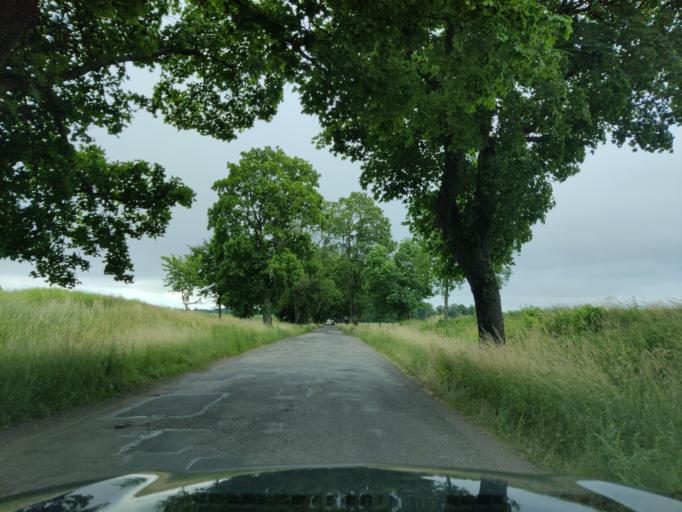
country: PL
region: Warmian-Masurian Voivodeship
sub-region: Powiat gizycki
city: Ryn
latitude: 53.9141
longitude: 21.5580
